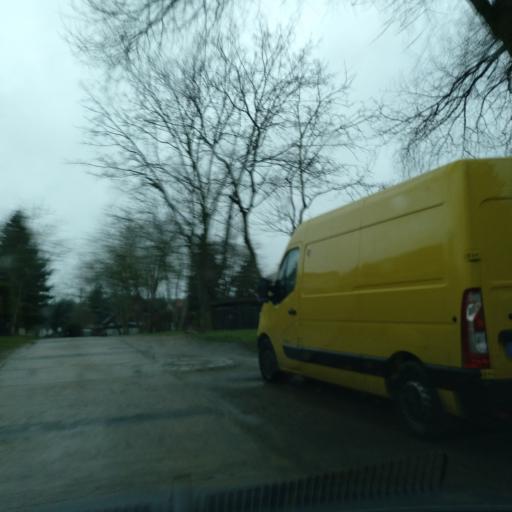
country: DE
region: Brandenburg
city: Neuenhagen
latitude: 52.5041
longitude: 13.6924
